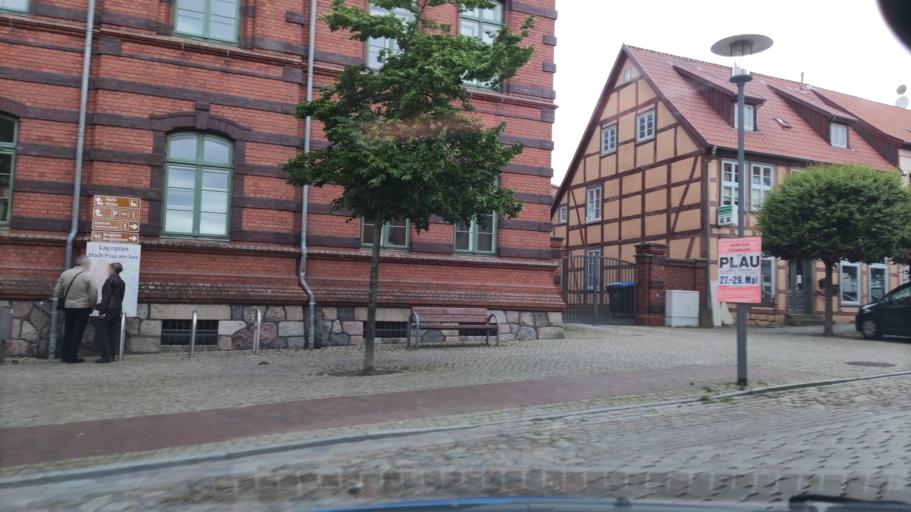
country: DE
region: Mecklenburg-Vorpommern
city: Plau am See
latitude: 53.4582
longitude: 12.2649
